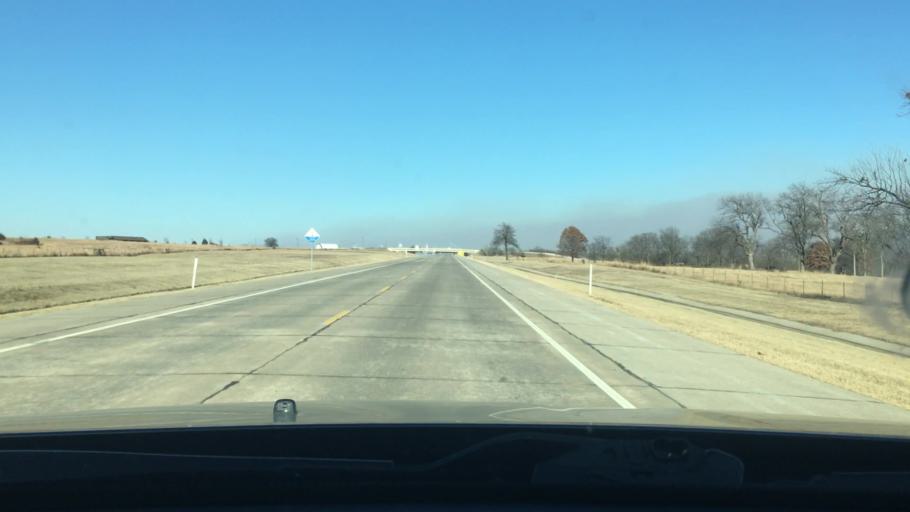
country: US
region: Oklahoma
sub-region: Murray County
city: Sulphur
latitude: 34.5584
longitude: -96.9374
